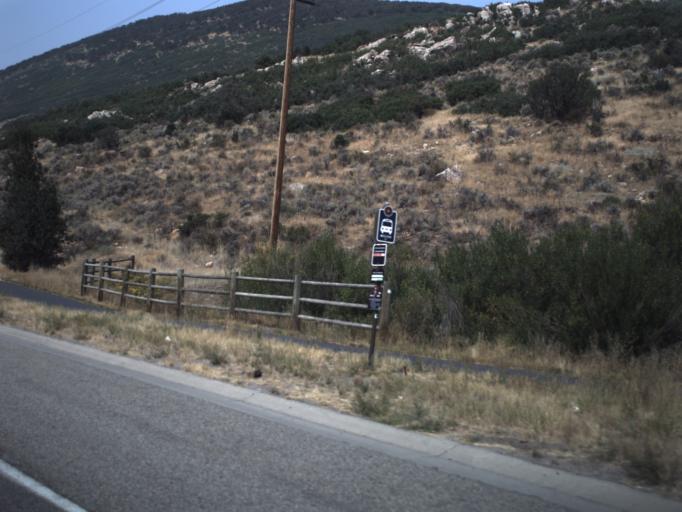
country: US
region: Utah
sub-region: Summit County
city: Snyderville
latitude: 40.6756
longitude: -111.5205
